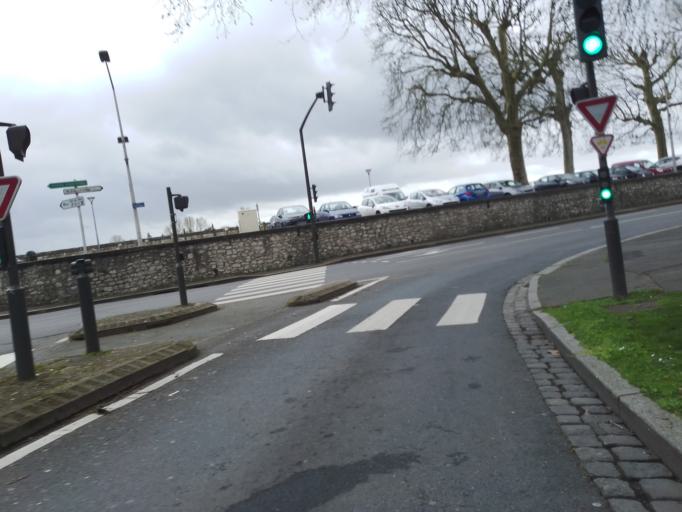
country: FR
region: Centre
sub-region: Departement du Loir-et-Cher
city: Blois
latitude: 47.5900
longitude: 1.3417
